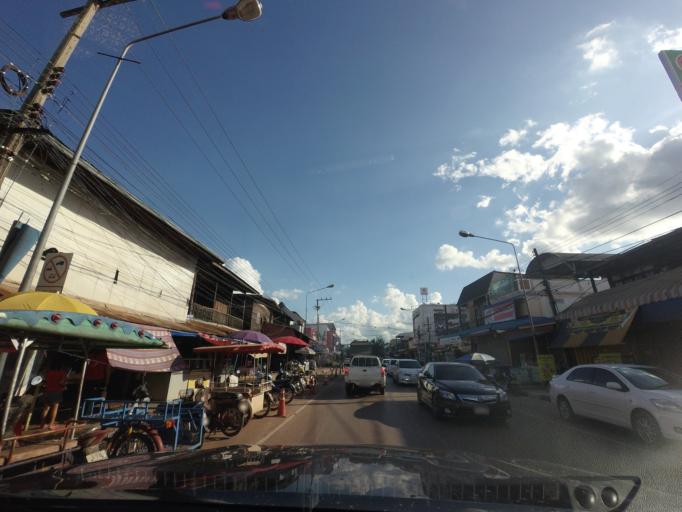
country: TH
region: Changwat Udon Thani
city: Ban Dung
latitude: 17.6968
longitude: 103.2590
